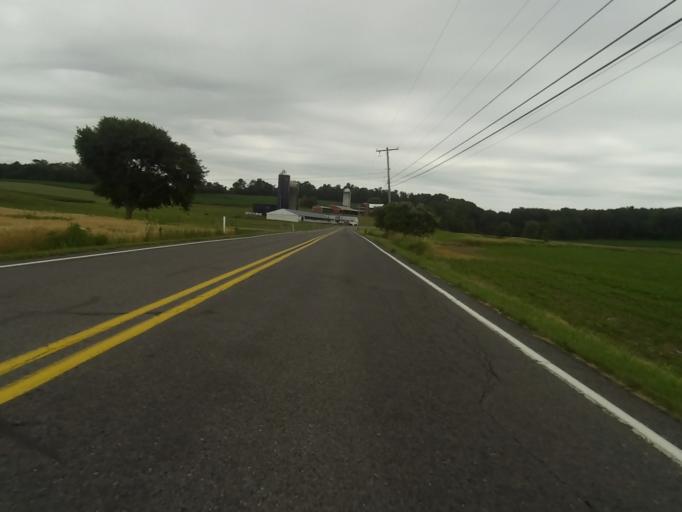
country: US
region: Pennsylvania
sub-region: Centre County
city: Pine Grove Mills
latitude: 40.7338
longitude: -77.9456
